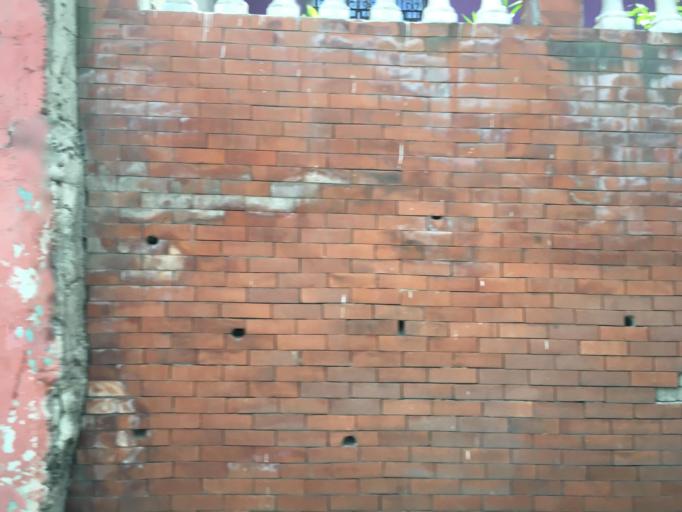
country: GT
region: Guatemala
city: Amatitlan
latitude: 14.4780
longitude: -90.6117
